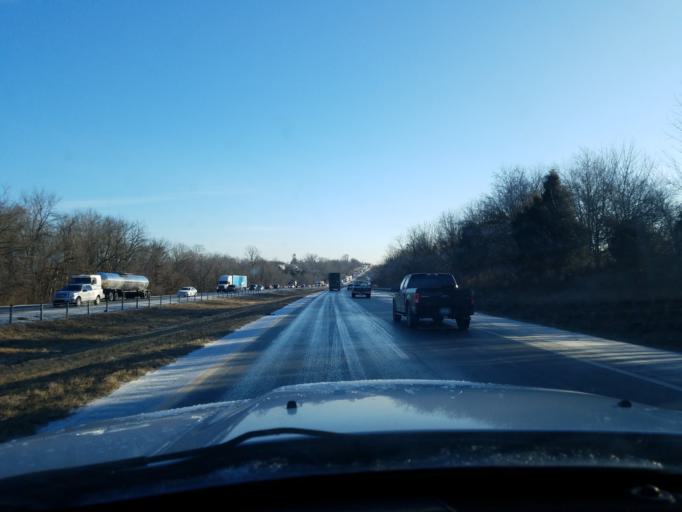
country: US
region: Kentucky
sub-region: Oldham County
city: Buckner
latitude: 38.3617
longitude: -85.4626
